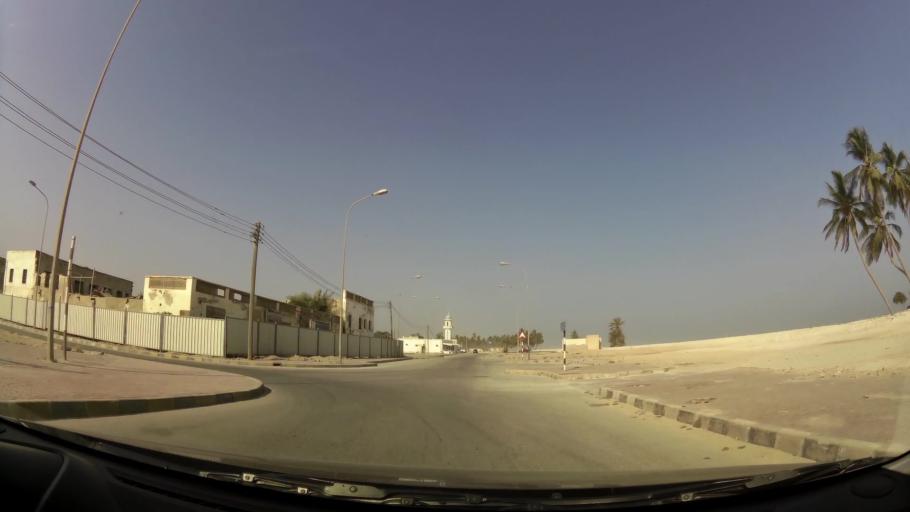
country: OM
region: Zufar
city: Salalah
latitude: 17.0009
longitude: 54.1058
